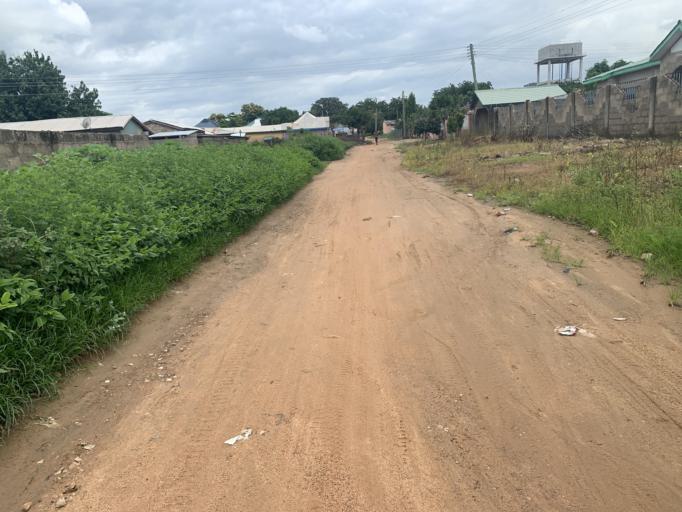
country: GH
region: Upper East
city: Navrongo
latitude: 10.9014
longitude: -1.0891
